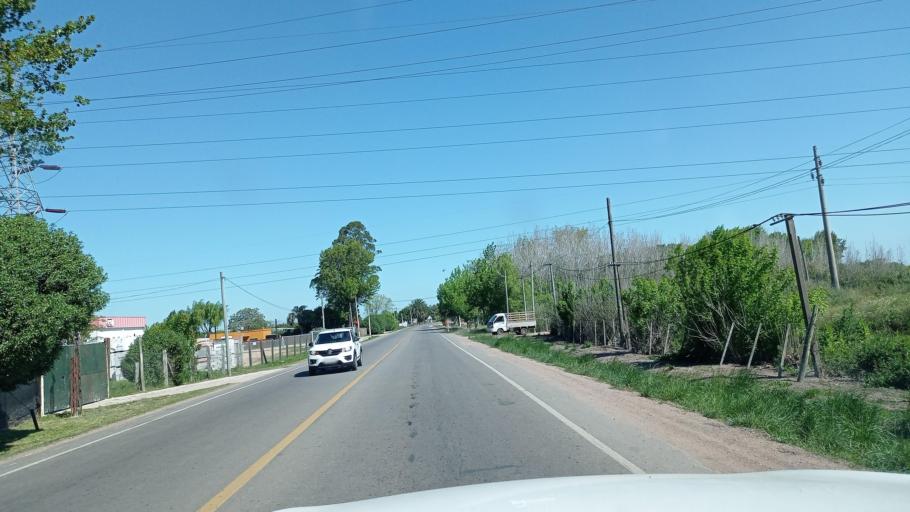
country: UY
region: Canelones
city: La Paz
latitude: -34.7854
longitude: -56.1672
